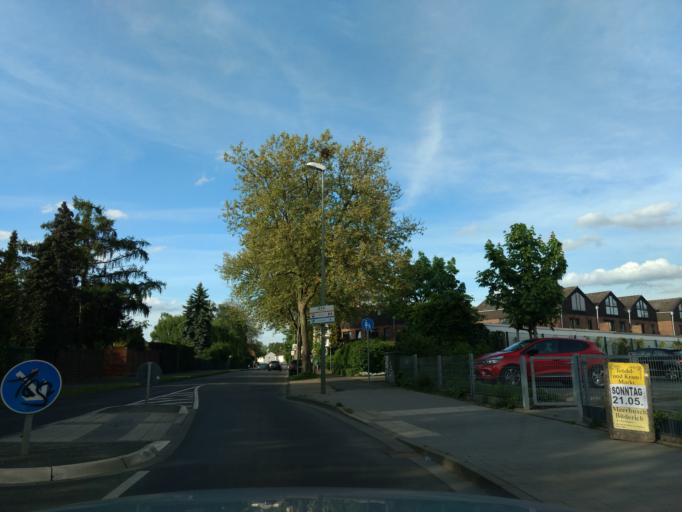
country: DE
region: North Rhine-Westphalia
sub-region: Regierungsbezirk Dusseldorf
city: Meerbusch
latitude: 51.2371
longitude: 6.6935
